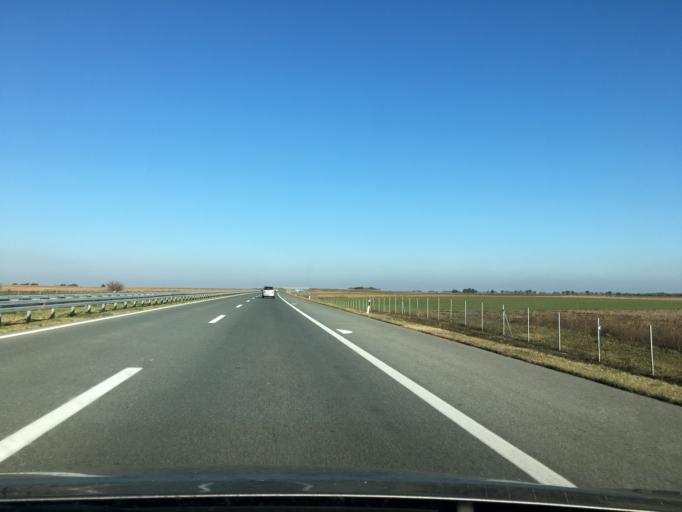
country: RS
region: Autonomna Pokrajina Vojvodina
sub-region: Severnobacki Okrug
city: Mali Igos
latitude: 45.7371
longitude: 19.7038
